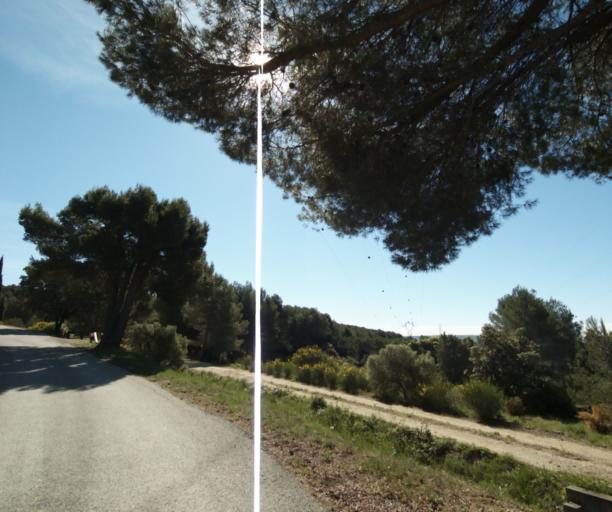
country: FR
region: Provence-Alpes-Cote d'Azur
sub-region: Departement des Bouches-du-Rhone
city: La Fare-les-Oliviers
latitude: 43.5137
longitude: 5.2042
